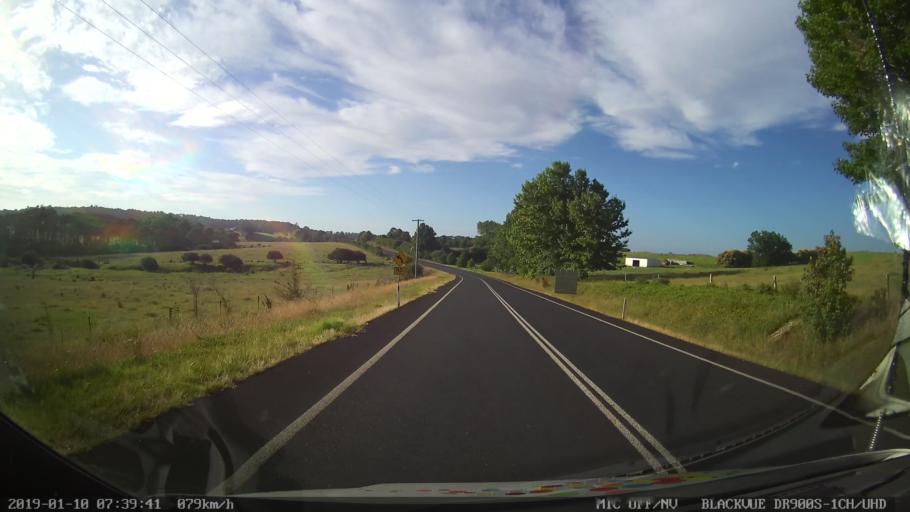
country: AU
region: New South Wales
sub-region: Bellingen
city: Dorrigo
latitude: -30.3597
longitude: 152.7197
